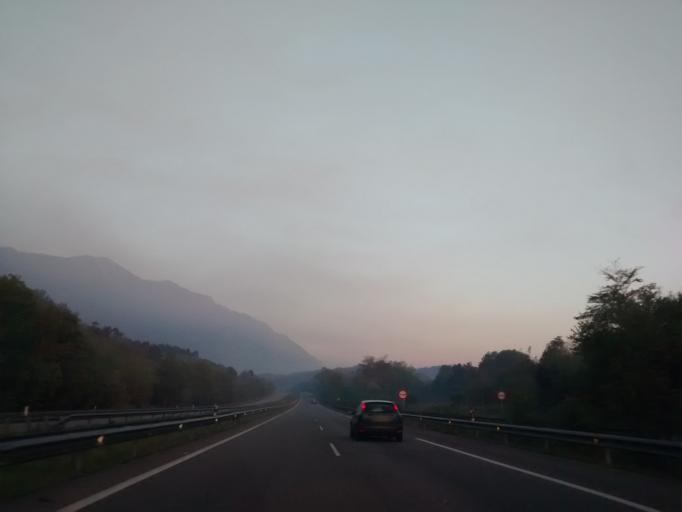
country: ES
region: Asturias
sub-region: Province of Asturias
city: Ribadesella
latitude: 43.4384
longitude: -4.9763
